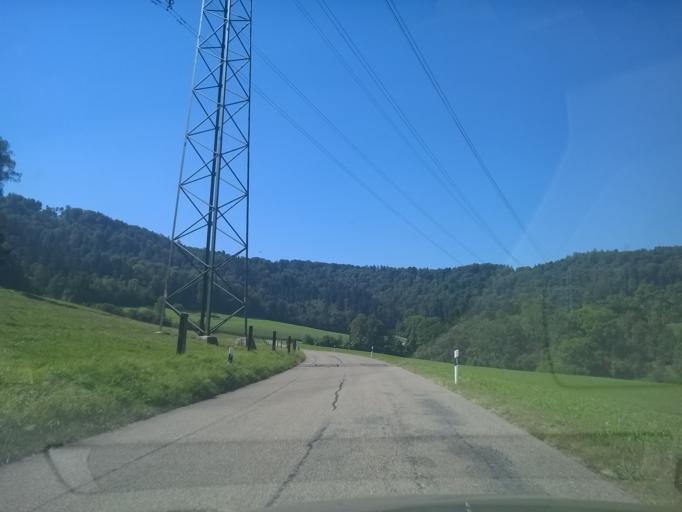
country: CH
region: Zurich
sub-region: Bezirk Winterthur
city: Pfungen
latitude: 47.5075
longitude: 8.6496
